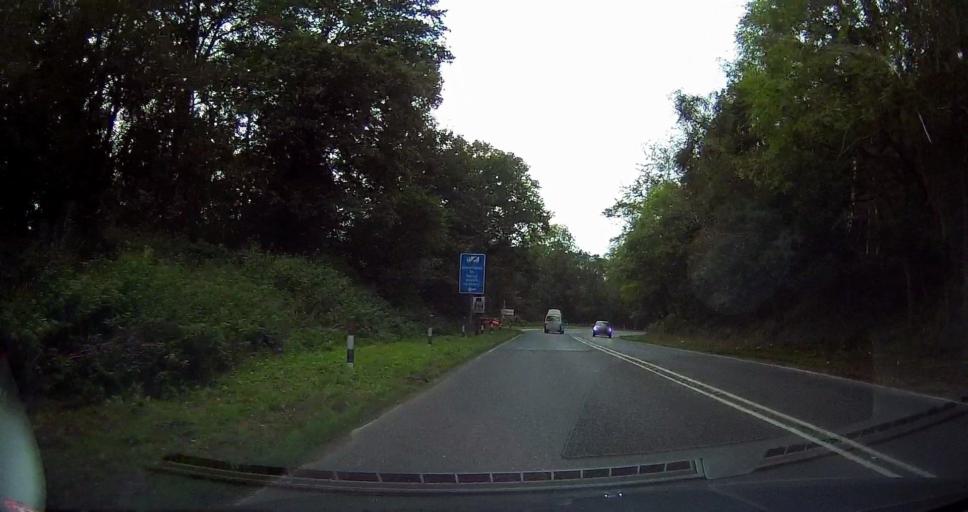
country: GB
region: England
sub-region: Kent
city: Harrietsham
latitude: 51.2487
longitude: 0.6391
